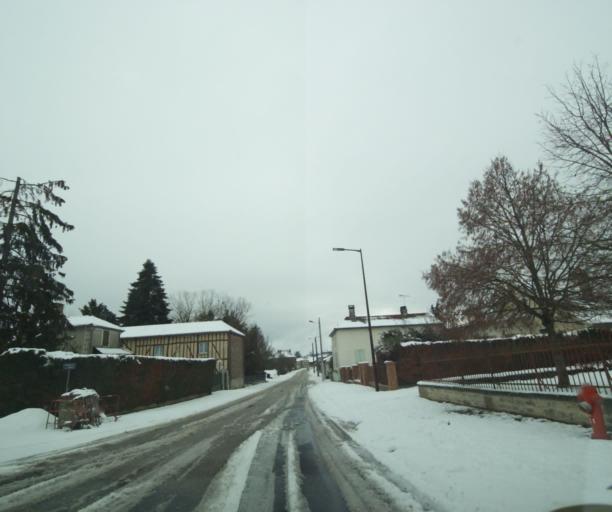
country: FR
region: Champagne-Ardenne
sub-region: Departement de la Haute-Marne
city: Montier-en-Der
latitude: 48.4344
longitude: 4.7260
